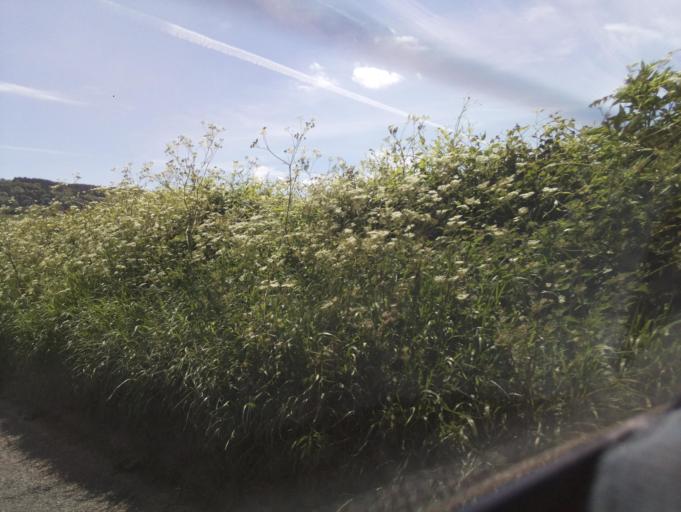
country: GB
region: Wales
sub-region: Monmouthshire
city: Monmouth
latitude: 51.7943
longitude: -2.7172
